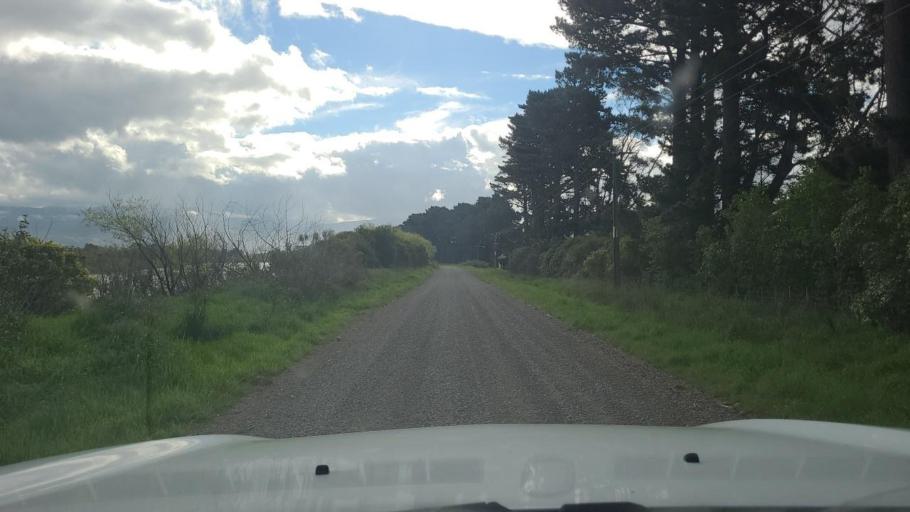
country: NZ
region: Wellington
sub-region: Upper Hutt City
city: Upper Hutt
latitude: -41.2932
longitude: 175.2239
